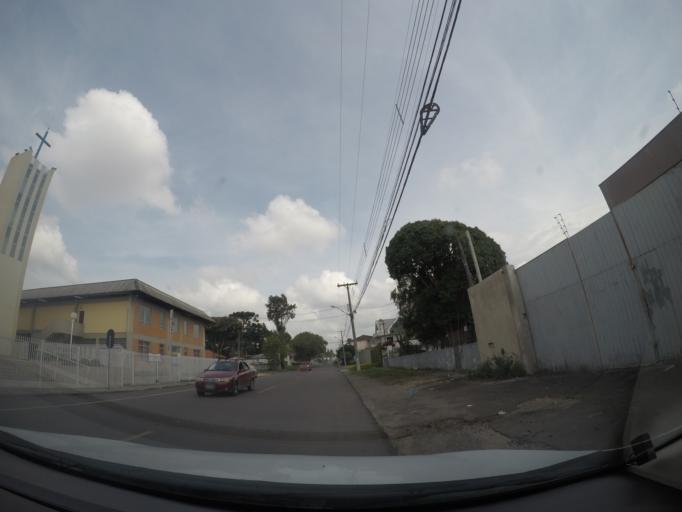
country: BR
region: Parana
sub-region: Curitiba
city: Curitiba
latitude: -25.4772
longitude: -49.2624
